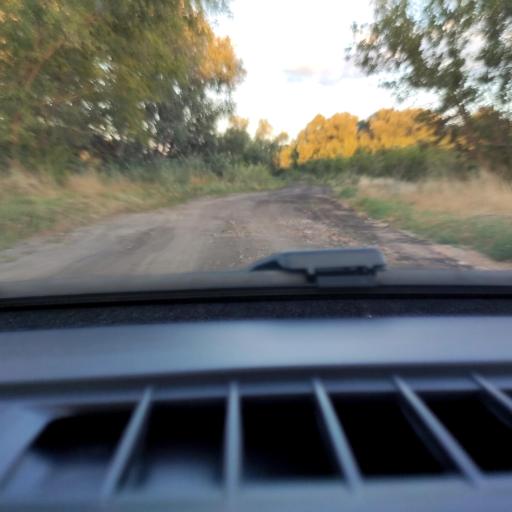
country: RU
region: Voronezj
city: Verkhnyaya Khava
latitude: 51.5925
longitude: 39.8463
